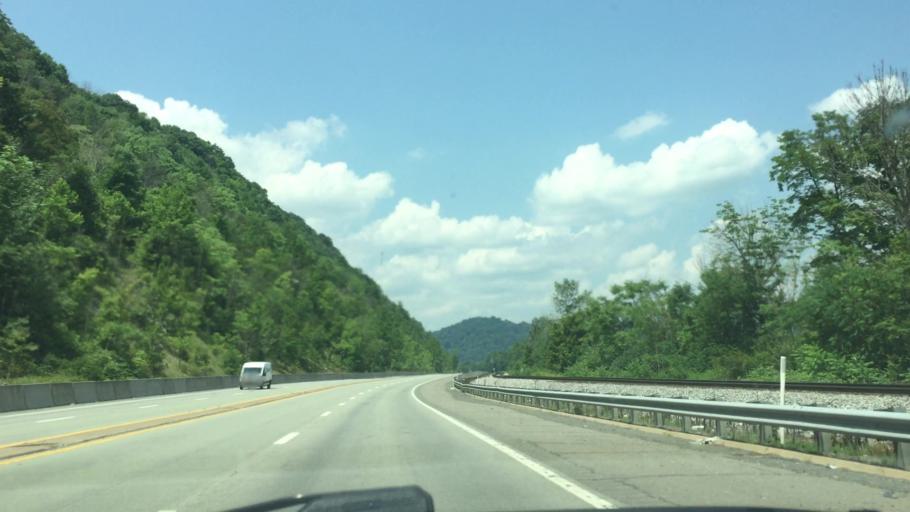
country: US
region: West Virginia
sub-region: Marshall County
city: Moundsville
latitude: 39.9079
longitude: -80.7723
